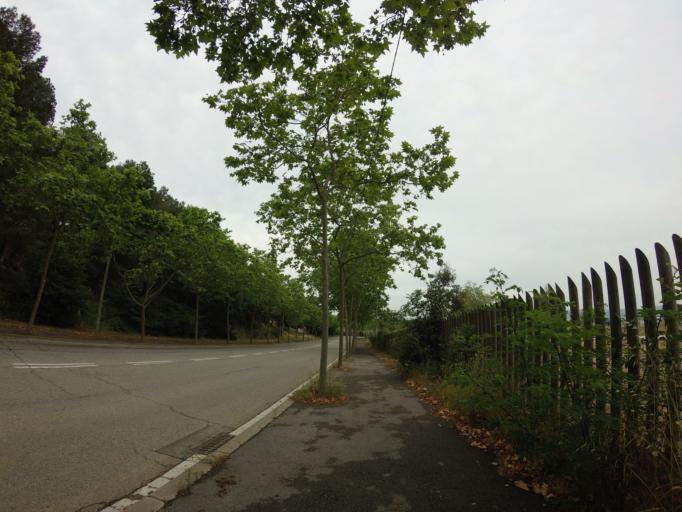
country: ES
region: Catalonia
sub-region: Provincia de Barcelona
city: Sants-Montjuic
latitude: 41.3609
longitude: 2.1589
